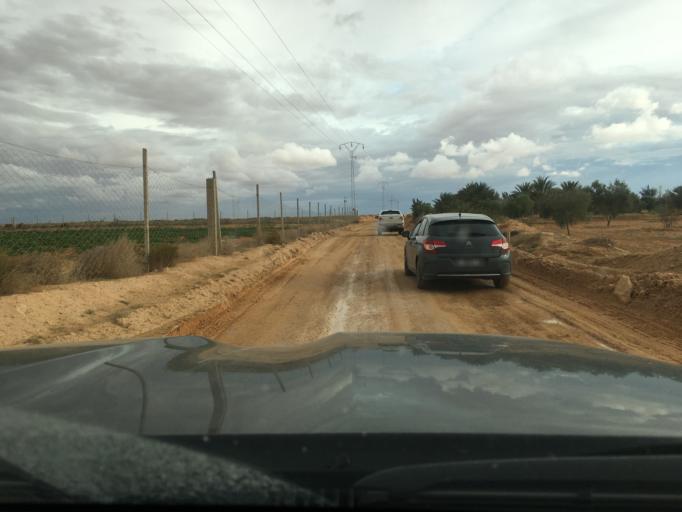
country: TN
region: Madanin
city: Medenine
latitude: 33.2760
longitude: 10.5610
